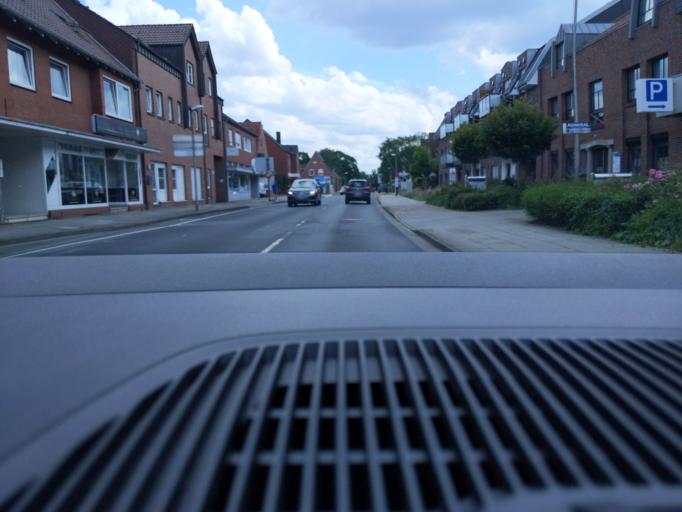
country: DE
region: Lower Saxony
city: Meppen
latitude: 52.6871
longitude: 7.2912
